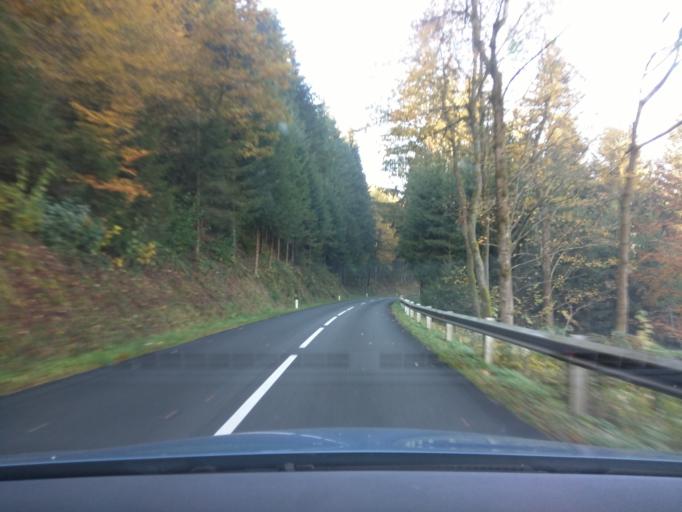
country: DE
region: Bavaria
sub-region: Lower Bavaria
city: Thyrnau
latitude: 48.5626
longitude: 13.5595
